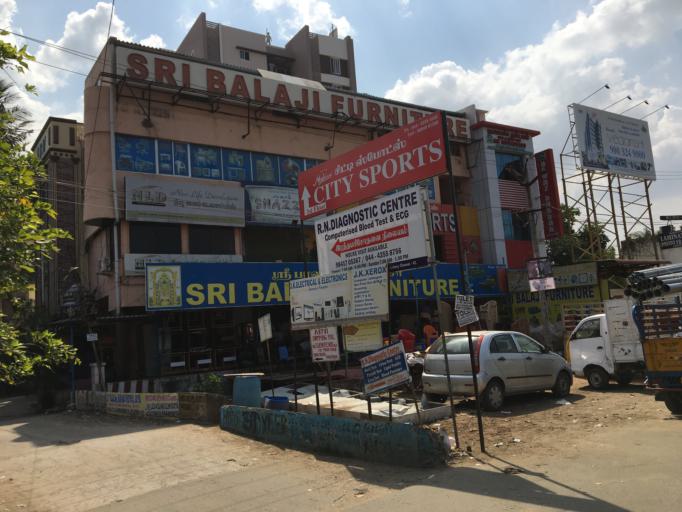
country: IN
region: Tamil Nadu
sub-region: Kancheepuram
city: Alandur
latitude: 12.9814
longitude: 80.2180
